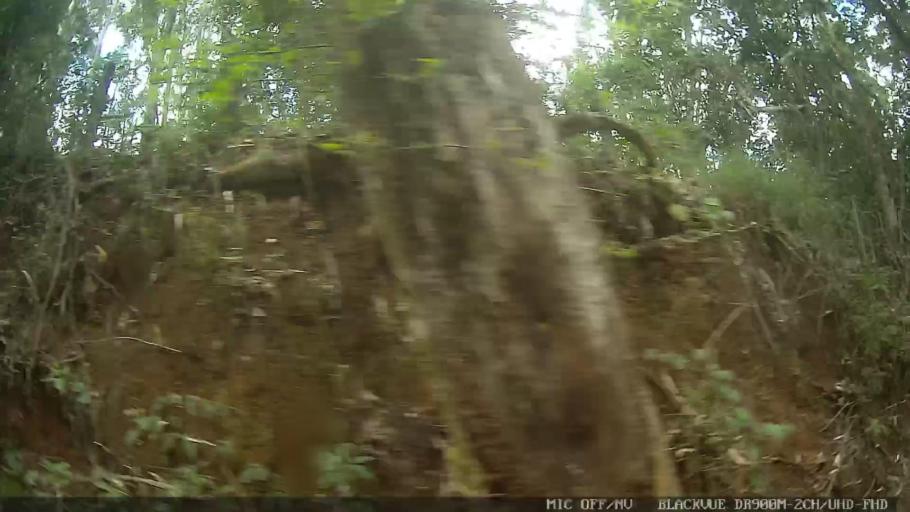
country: BR
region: Sao Paulo
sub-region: Braganca Paulista
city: Braganca Paulista
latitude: -23.0246
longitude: -46.4666
